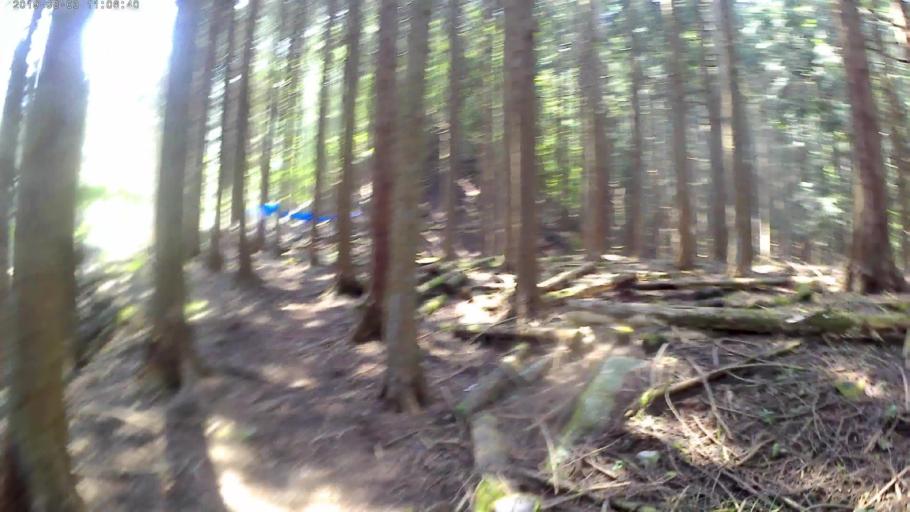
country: JP
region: Yamanashi
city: Enzan
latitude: 35.6175
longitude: 138.7743
